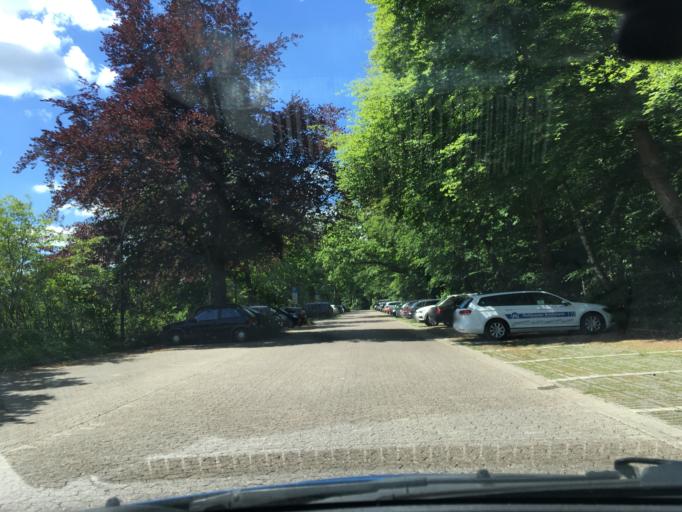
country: DE
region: Lower Saxony
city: Uelzen
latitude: 52.9750
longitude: 10.5358
